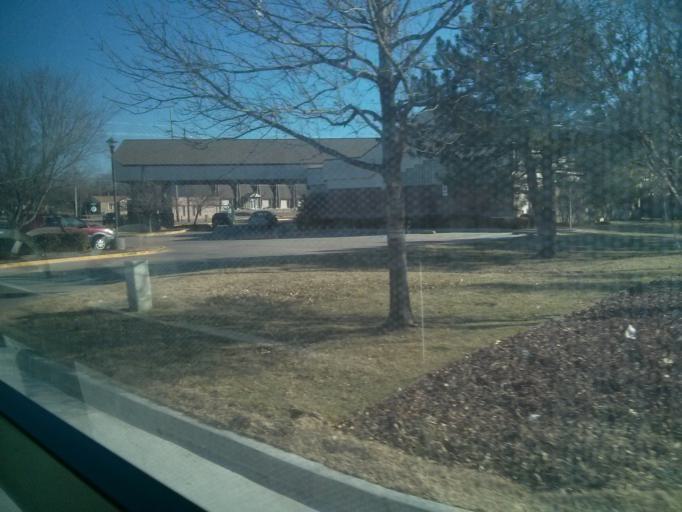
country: US
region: Oklahoma
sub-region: Tulsa County
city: Tulsa
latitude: 36.1762
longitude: -95.9807
